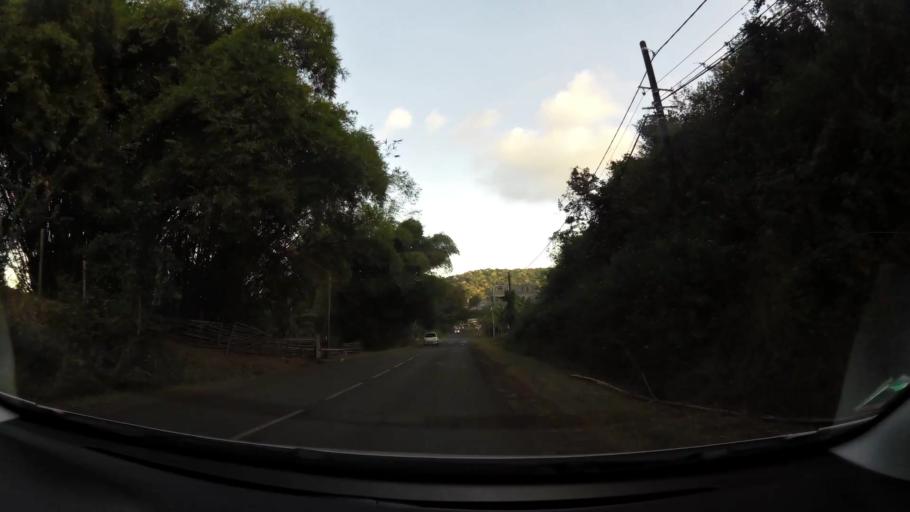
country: YT
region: Dembeni
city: Dembeni
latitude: -12.8640
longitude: 45.1982
